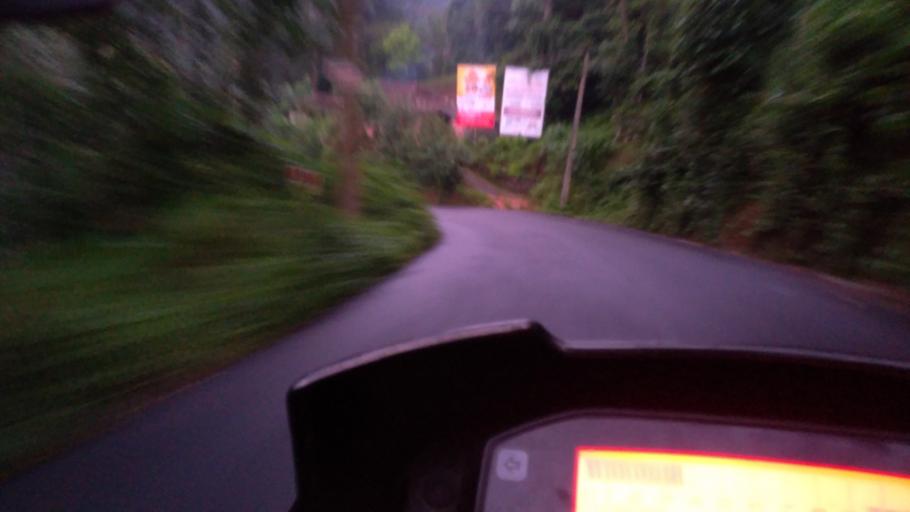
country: IN
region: Kerala
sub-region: Idukki
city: Munnar
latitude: 9.9629
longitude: 77.0687
